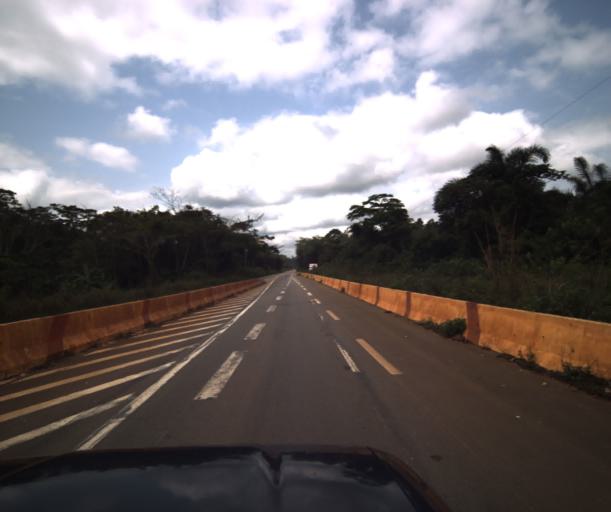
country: CM
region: Centre
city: Mbankomo
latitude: 3.7942
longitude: 11.3297
